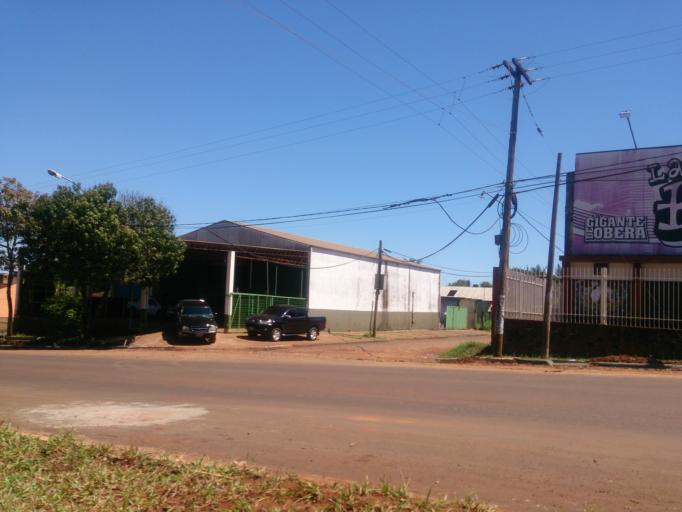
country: AR
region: Misiones
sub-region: Departamento de Obera
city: Obera
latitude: -27.4949
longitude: -55.1121
